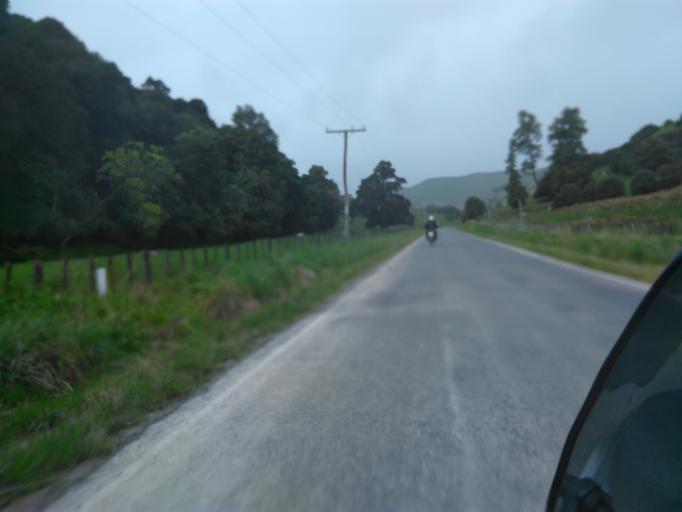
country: NZ
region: Gisborne
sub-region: Gisborne District
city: Gisborne
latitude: -38.6386
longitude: 177.7016
